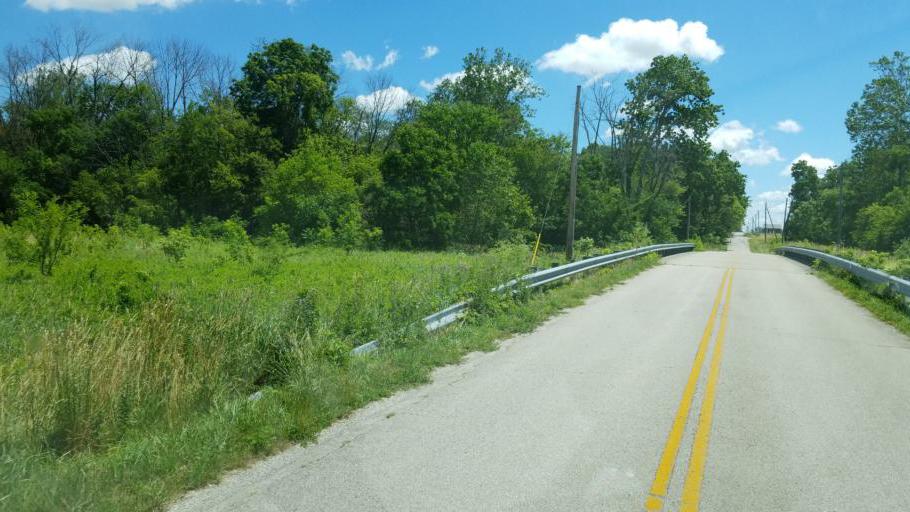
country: US
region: Ohio
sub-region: Crawford County
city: Bucyrus
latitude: 40.7402
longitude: -82.9128
